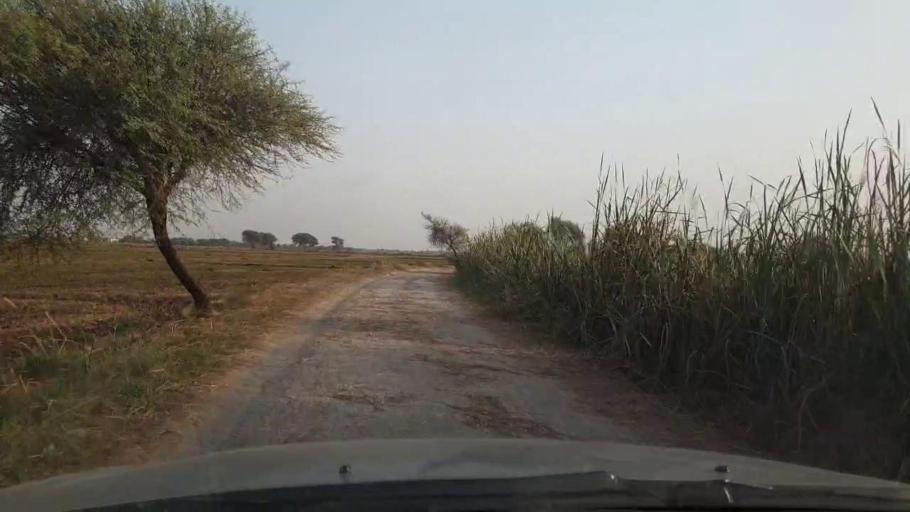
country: PK
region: Sindh
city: Tando Muhammad Khan
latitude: 25.0257
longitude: 68.4384
